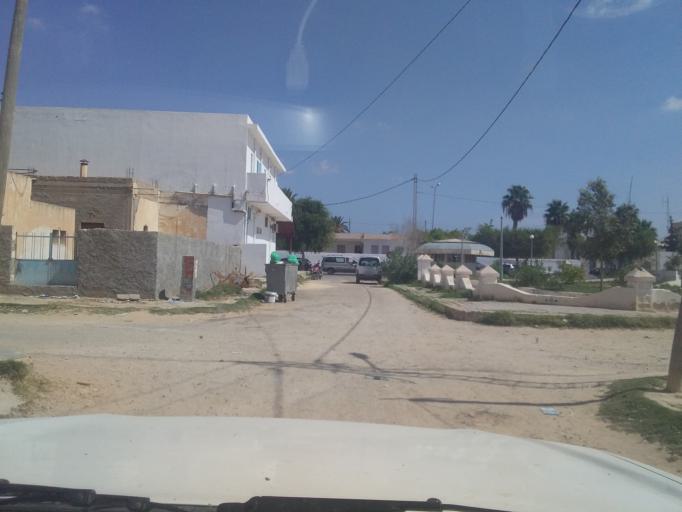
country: TN
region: Qabis
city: Matmata
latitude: 33.6153
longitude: 10.2893
